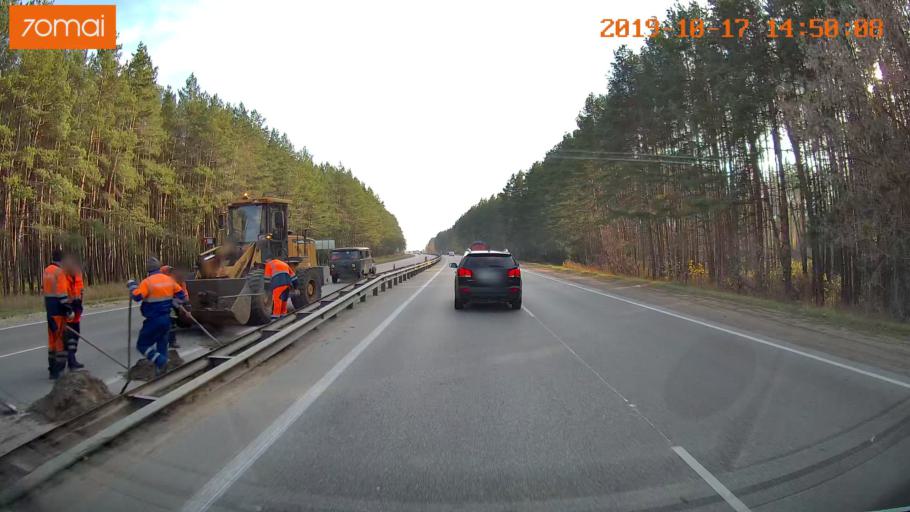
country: RU
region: Rjazan
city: Polyany
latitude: 54.7379
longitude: 39.8410
